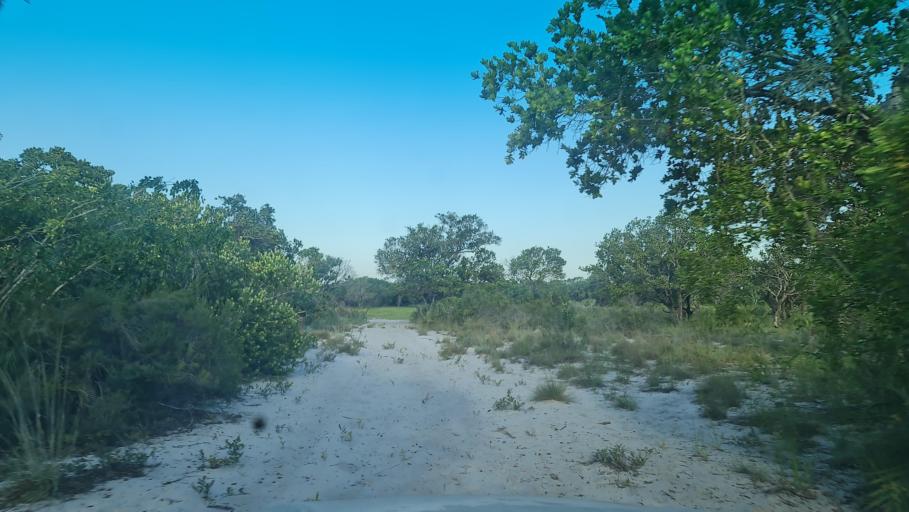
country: MZ
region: Gaza
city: Macia
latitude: -25.2271
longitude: 33.0225
